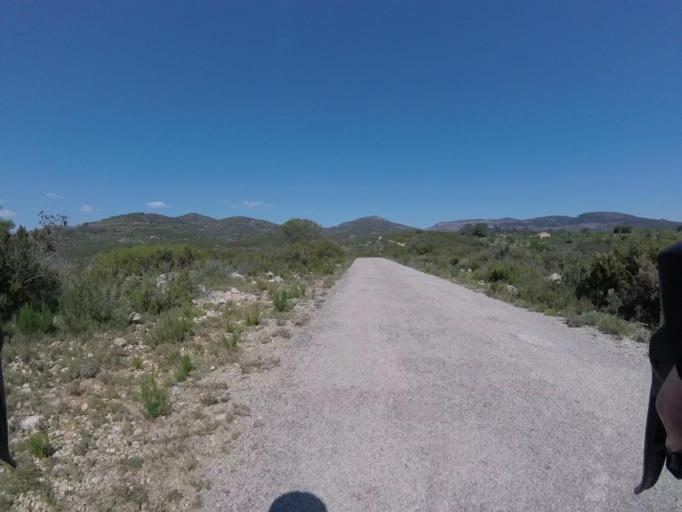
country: ES
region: Valencia
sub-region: Provincia de Castello
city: Sierra-Engarceran
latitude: 40.2348
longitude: -0.0262
